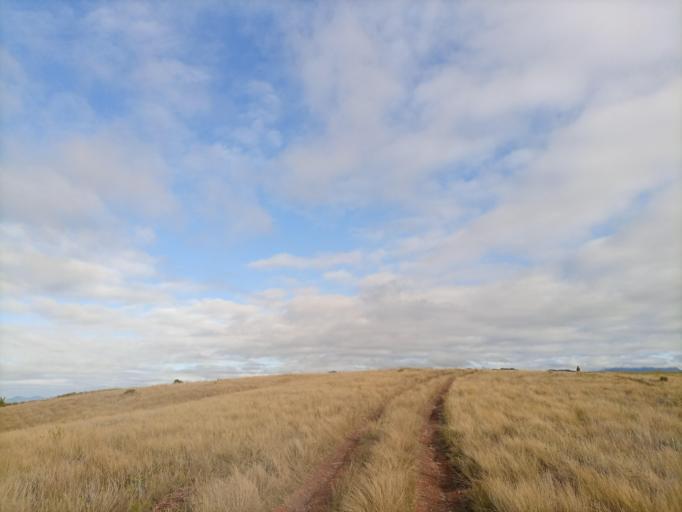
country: MG
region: Anosy
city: Fort Dauphin
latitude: -24.3148
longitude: 47.2552
